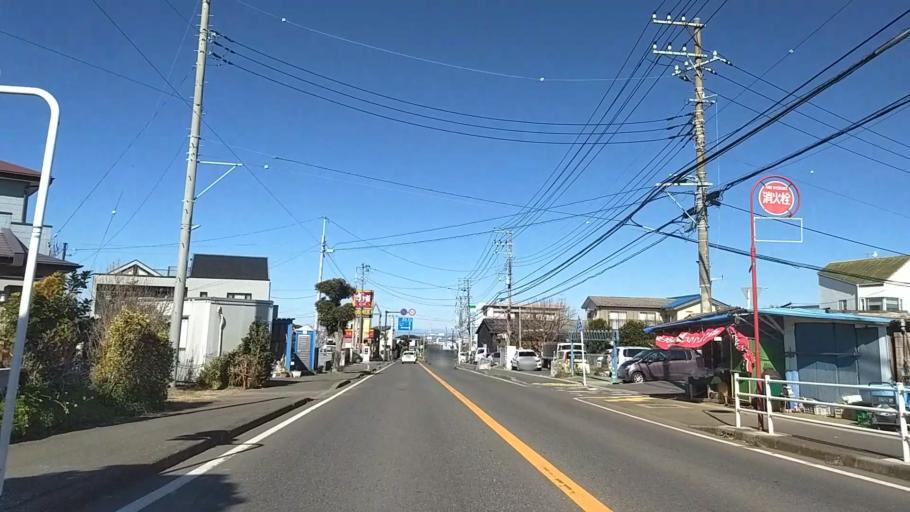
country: JP
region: Kanagawa
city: Miura
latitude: 35.1733
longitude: 139.6356
